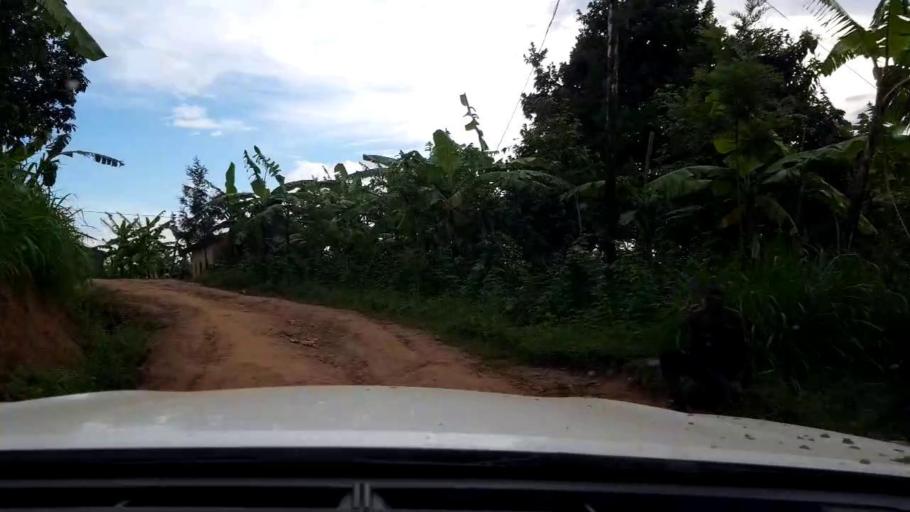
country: RW
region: Western Province
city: Kibuye
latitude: -2.0049
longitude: 29.3717
